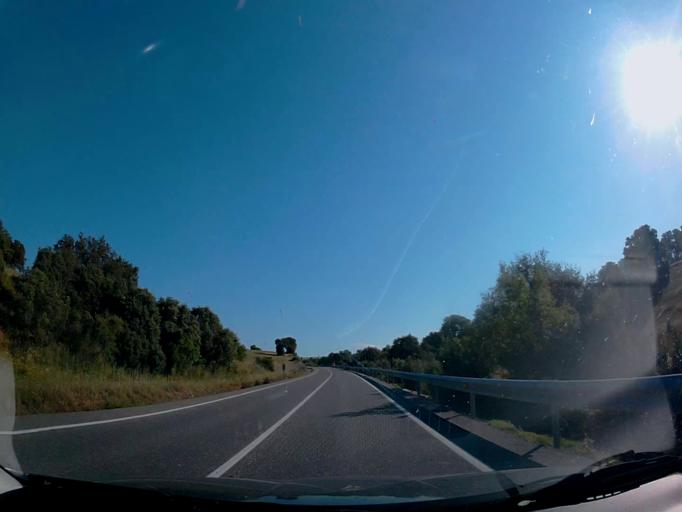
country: ES
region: Castille-La Mancha
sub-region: Province of Toledo
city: Escalona
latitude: 40.1966
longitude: -4.4001
